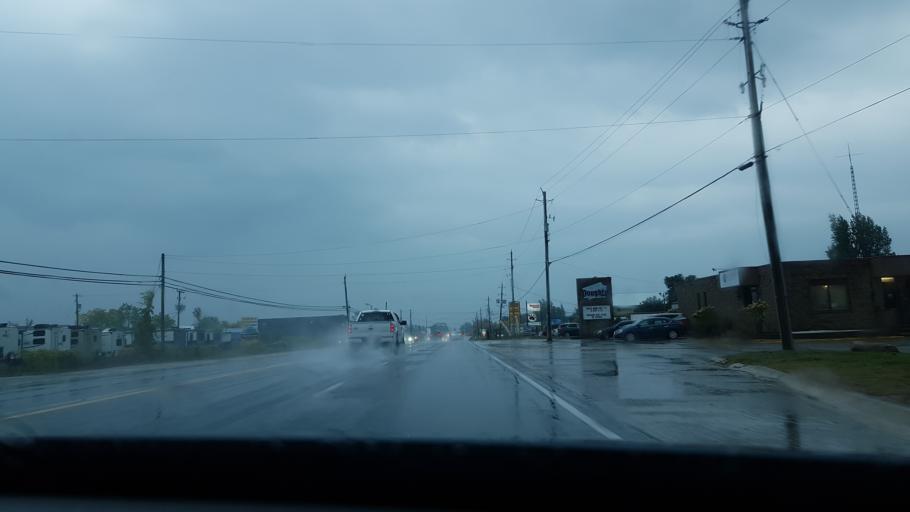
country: CA
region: Ontario
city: Peterborough
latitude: 44.3405
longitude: -78.3530
